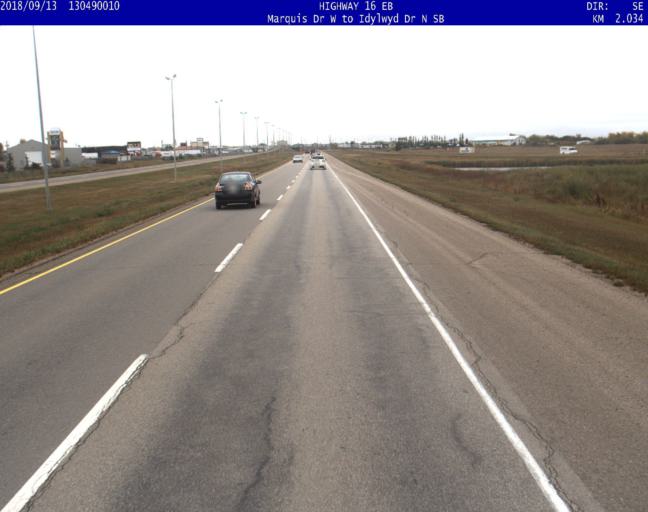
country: CA
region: Saskatchewan
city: Saskatoon
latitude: 52.1892
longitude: -106.6840
